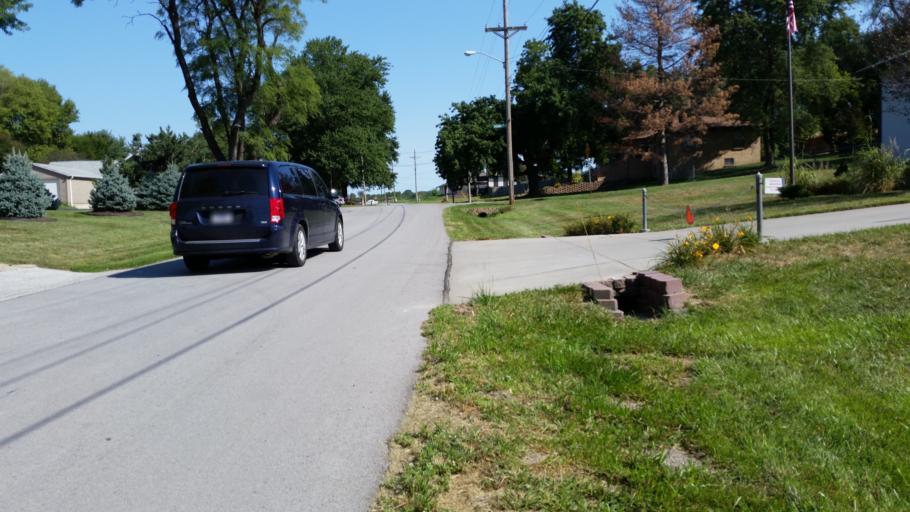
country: US
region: Nebraska
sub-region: Sarpy County
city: Bellevue
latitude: 41.1743
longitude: -95.9280
